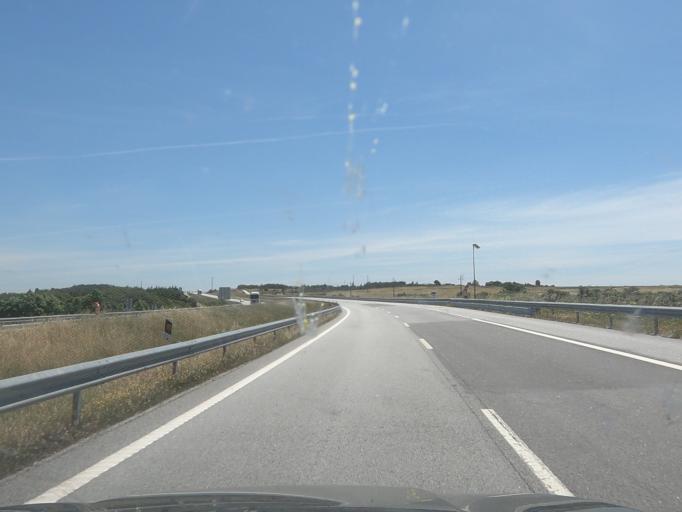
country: ES
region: Castille and Leon
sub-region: Provincia de Salamanca
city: Fuentes de Onoro
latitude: 40.6043
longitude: -6.9695
